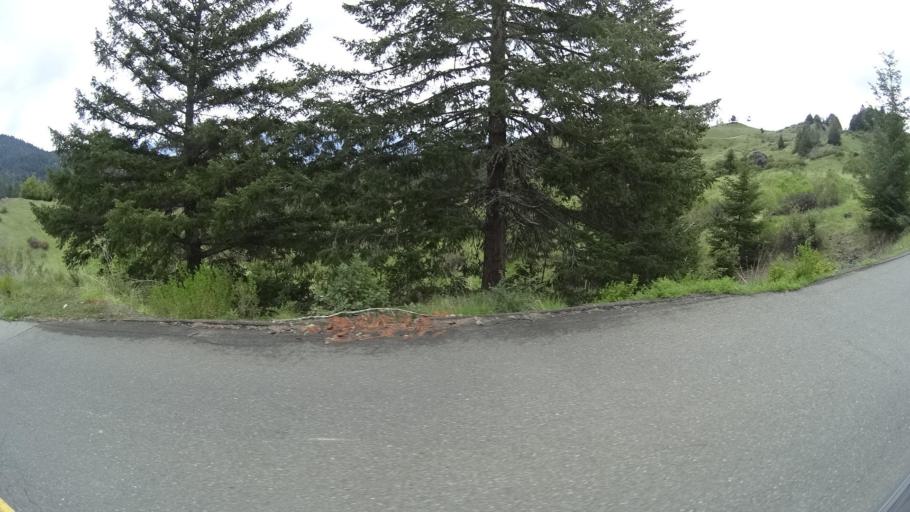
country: US
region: California
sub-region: Humboldt County
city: Redway
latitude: 40.1120
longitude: -123.6725
